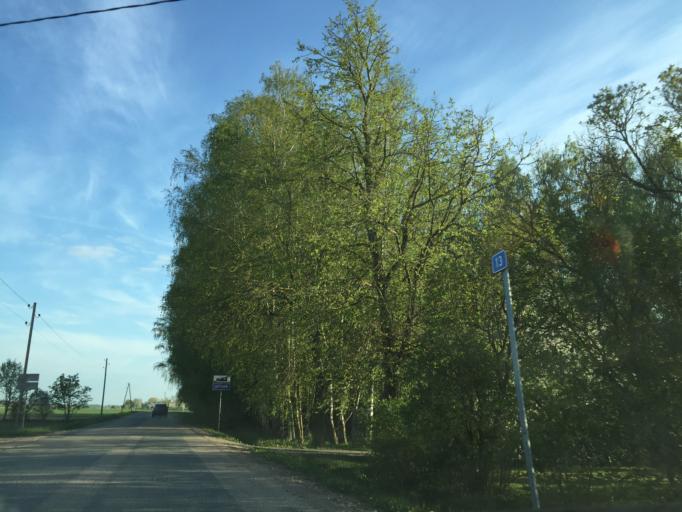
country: LV
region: Bauskas Rajons
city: Bauska
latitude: 56.3040
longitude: 24.2613
